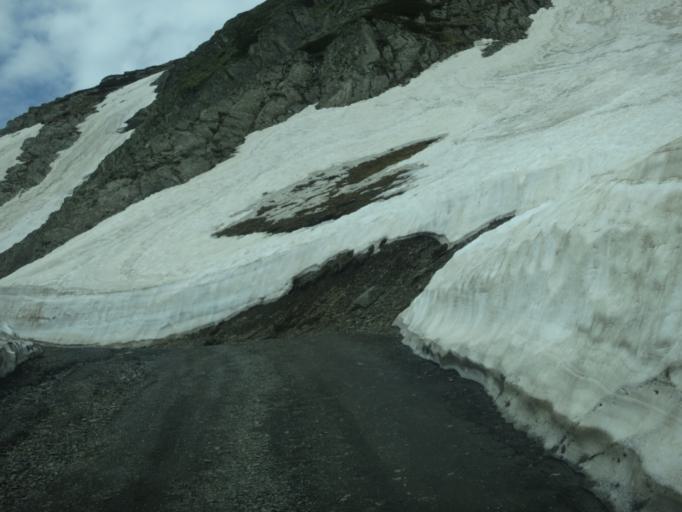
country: GE
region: Kakheti
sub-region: Telavi
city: Telavi
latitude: 42.2840
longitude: 45.5023
